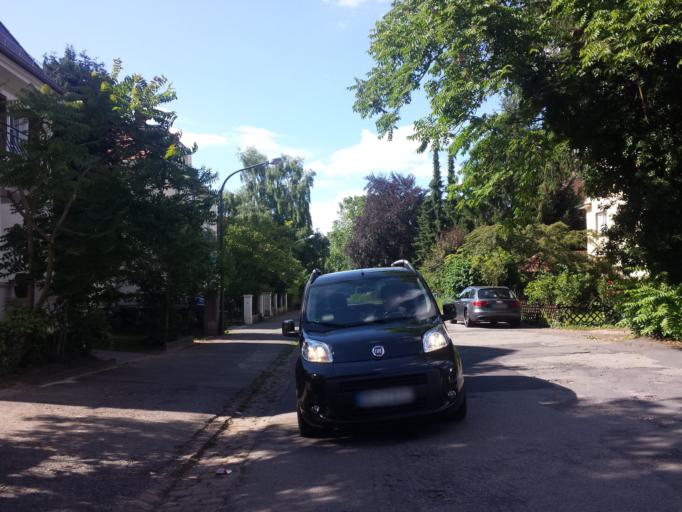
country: DE
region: Baden-Wuerttemberg
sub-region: Karlsruhe Region
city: Heidelberg
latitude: 49.4176
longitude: 8.6818
